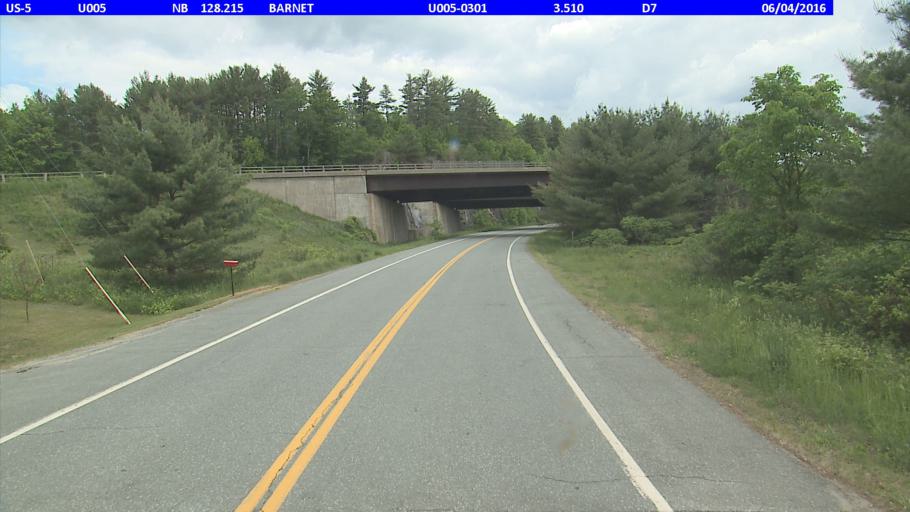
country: US
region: Vermont
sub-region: Caledonia County
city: Saint Johnsbury
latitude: 44.2996
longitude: -72.0461
